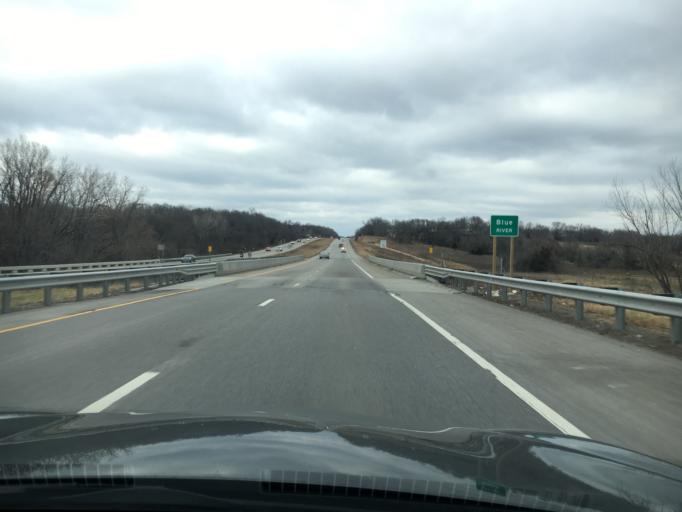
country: US
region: Missouri
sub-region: Cass County
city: Belton
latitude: 38.8113
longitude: -94.6754
